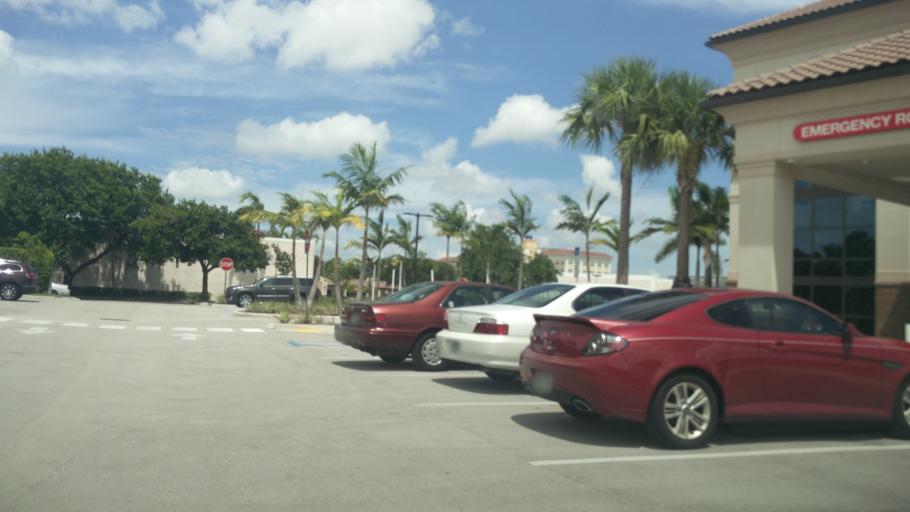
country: US
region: Florida
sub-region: Broward County
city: Davie
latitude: 26.0778
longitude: -80.2512
